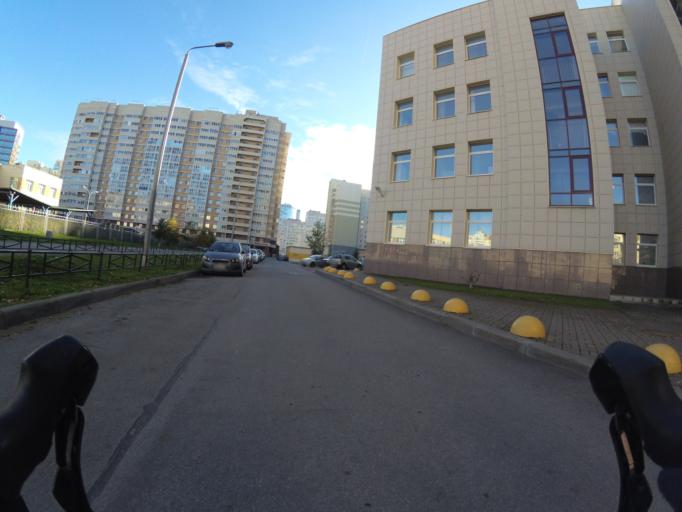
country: RU
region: Leningrad
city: Untolovo
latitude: 59.9981
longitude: 30.2033
